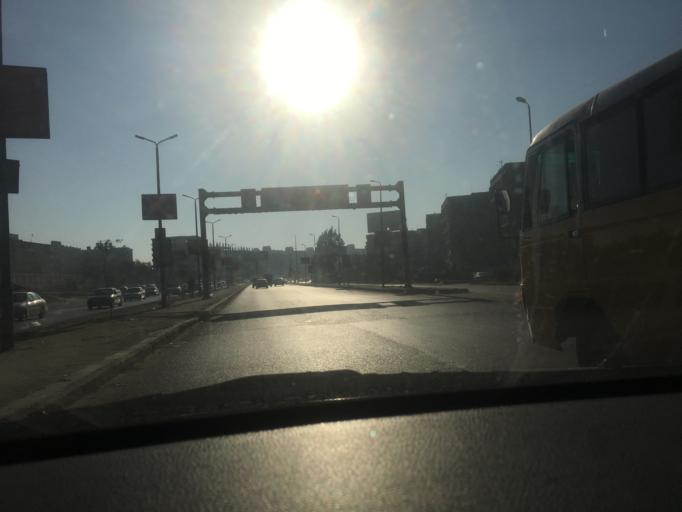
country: EG
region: Al Jizah
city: Al Jizah
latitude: 29.9898
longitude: 31.2854
